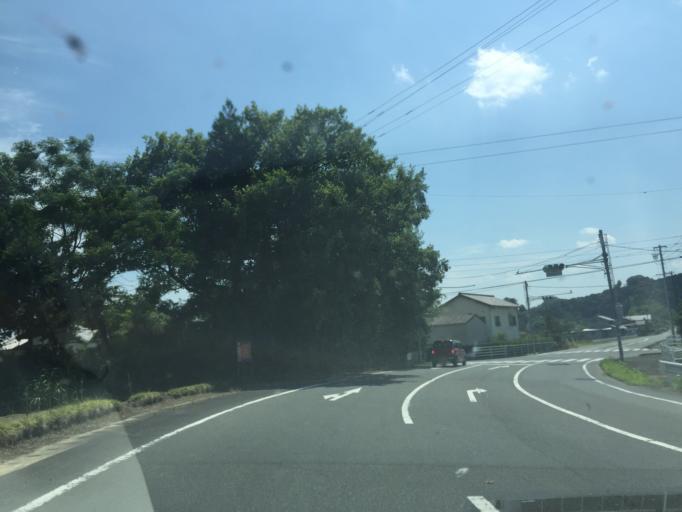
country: JP
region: Shizuoka
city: Kakegawa
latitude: 34.7970
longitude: 137.9803
